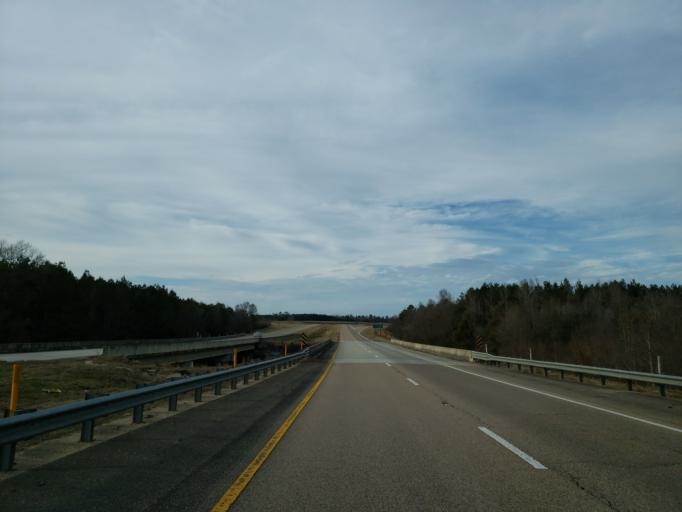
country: US
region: Mississippi
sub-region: Wayne County
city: Waynesboro
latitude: 31.6753
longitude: -88.6097
